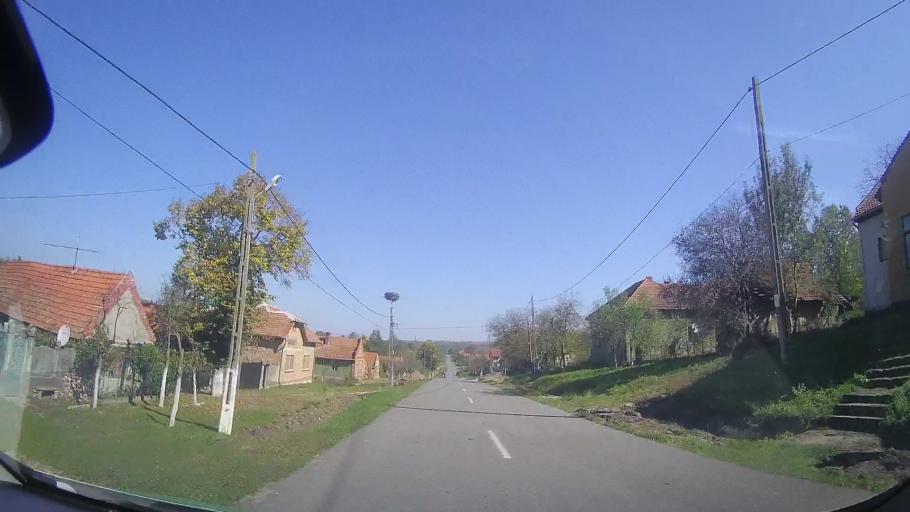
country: RO
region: Timis
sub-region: Comuna Balint
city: Balint
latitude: 45.8470
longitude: 21.8651
